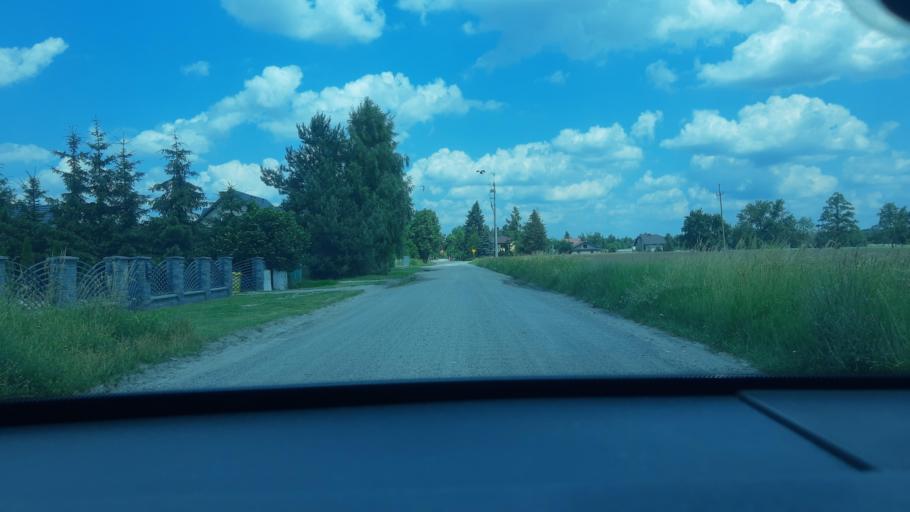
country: PL
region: Lodz Voivodeship
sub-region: Powiat sieradzki
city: Burzenin
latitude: 51.4560
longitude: 18.8456
